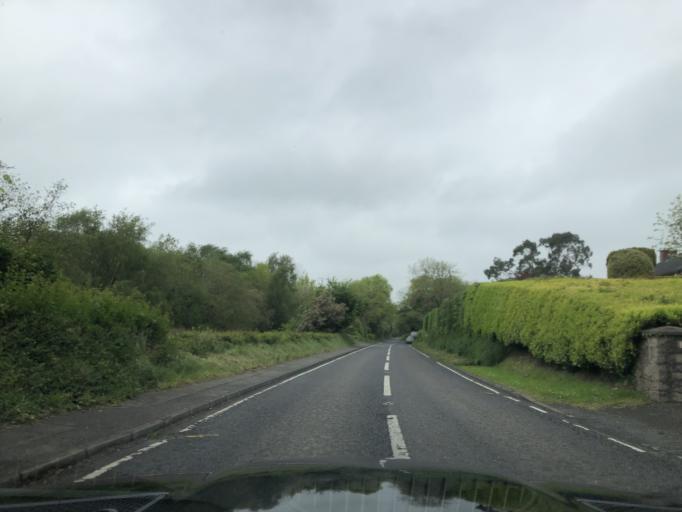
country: GB
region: Northern Ireland
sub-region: Down District
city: Downpatrick
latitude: 54.3471
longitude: -5.7005
